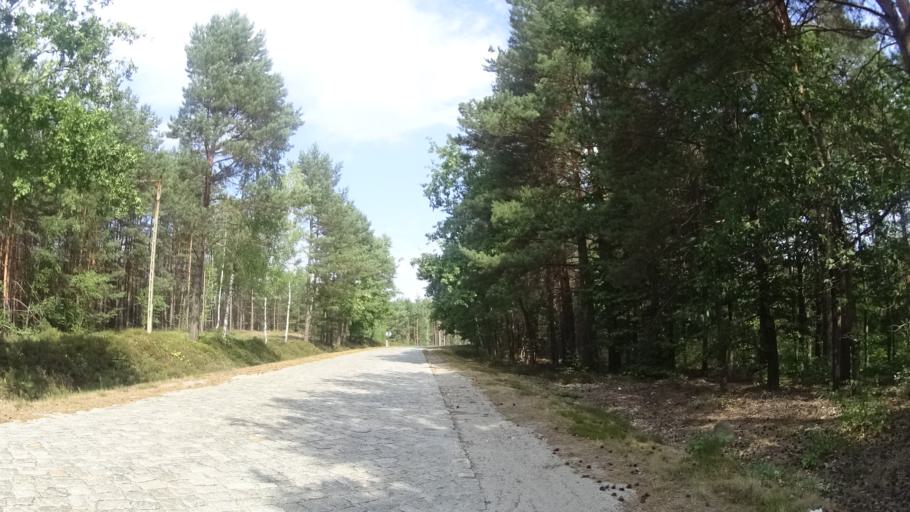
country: PL
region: Lubusz
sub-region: Powiat zarski
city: Leknica
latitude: 51.5266
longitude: 14.8199
